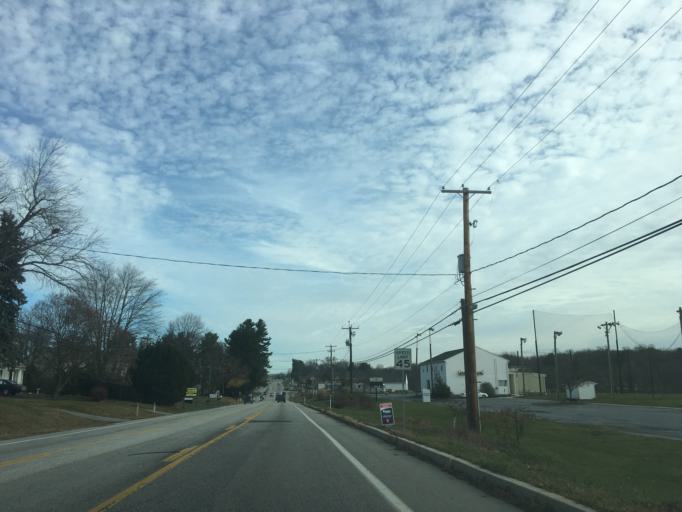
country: US
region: Pennsylvania
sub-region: Dauphin County
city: Lawrence Park
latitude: 40.3356
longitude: -76.8307
